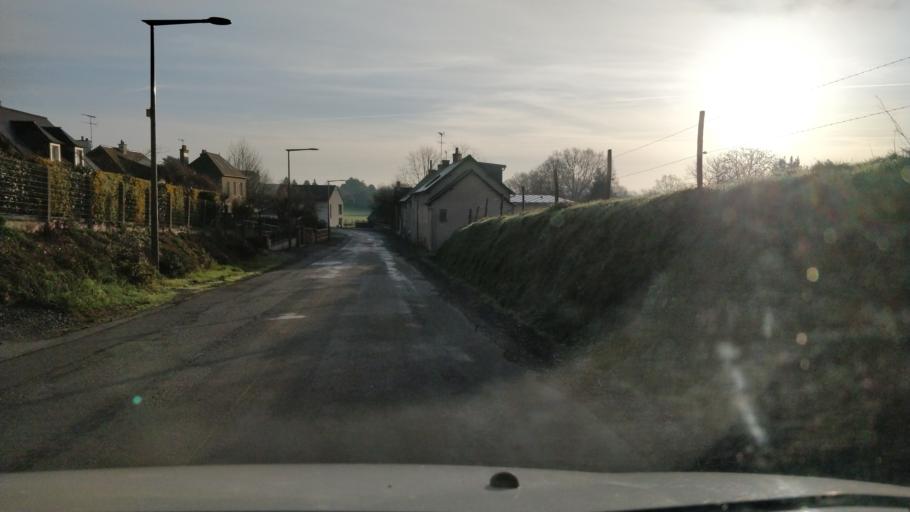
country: FR
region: Brittany
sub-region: Departement d'Ille-et-Vilaine
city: Bais
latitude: 48.0086
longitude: -1.2959
